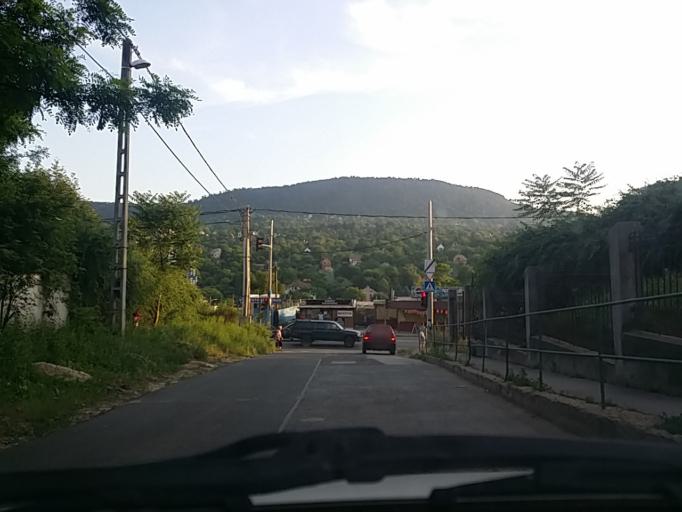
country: HU
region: Pest
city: Urom
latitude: 47.5823
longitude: 19.0019
